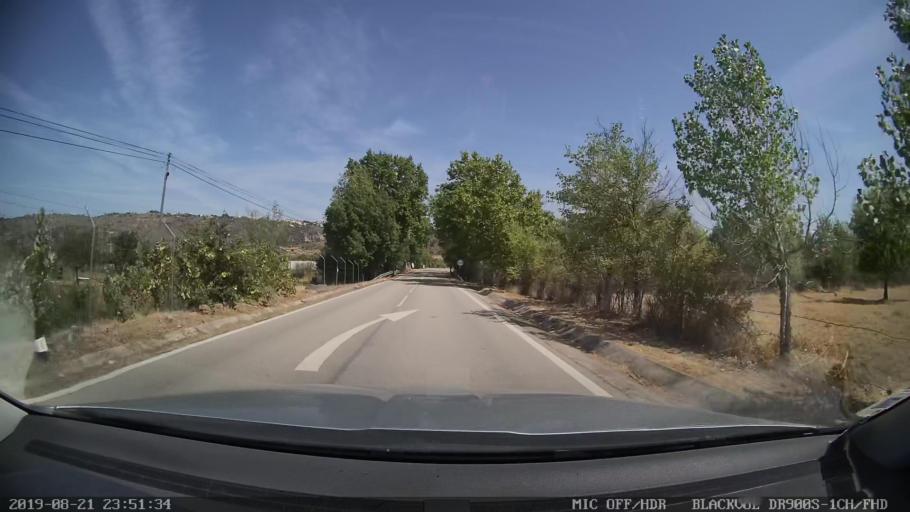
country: PT
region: Castelo Branco
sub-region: Idanha-A-Nova
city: Idanha-a-Nova
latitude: 39.9037
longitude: -7.2341
